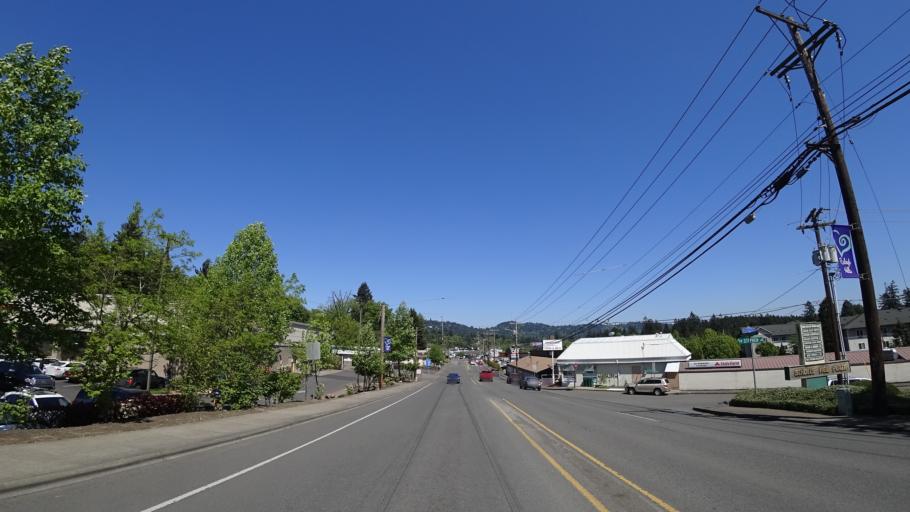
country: US
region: Oregon
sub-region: Washington County
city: Raleigh Hills
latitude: 45.4850
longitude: -122.7515
